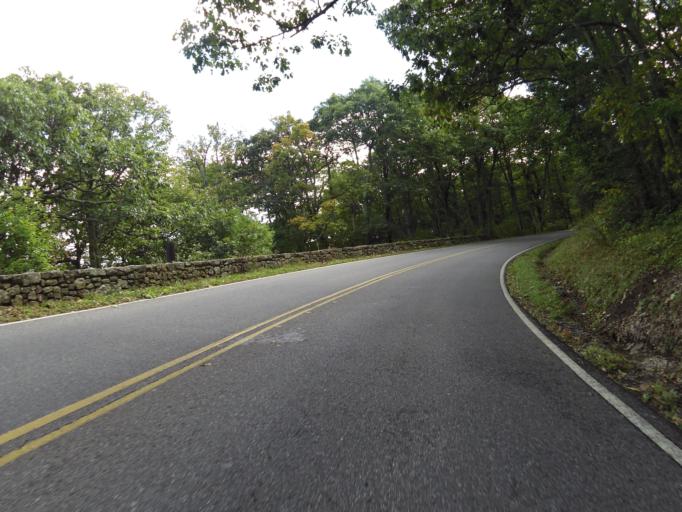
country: US
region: Virginia
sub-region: Page County
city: Luray
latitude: 38.5961
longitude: -78.3599
